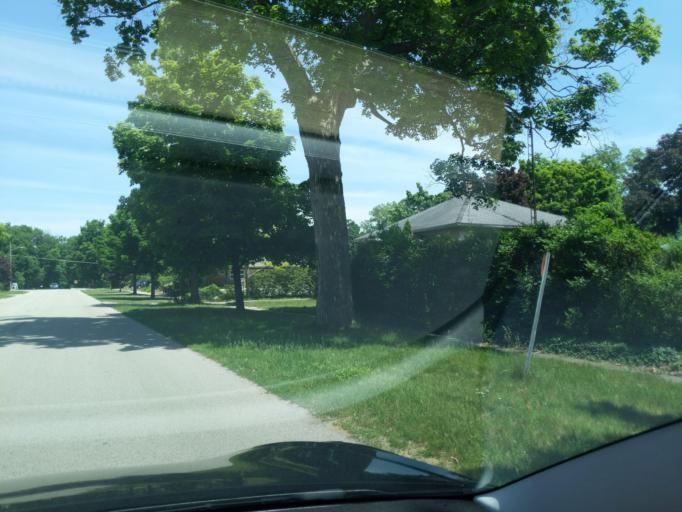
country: US
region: Michigan
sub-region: Muskegon County
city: Montague
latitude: 43.4159
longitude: -86.3593
